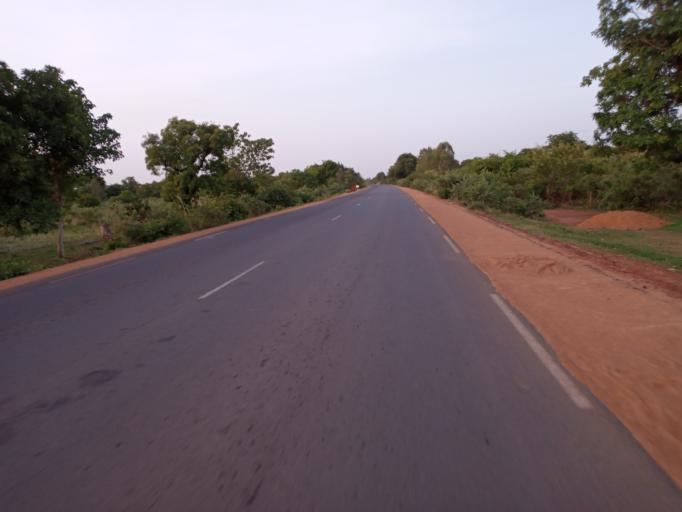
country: ML
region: Bamako
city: Bamako
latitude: 12.2880
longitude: -8.1722
